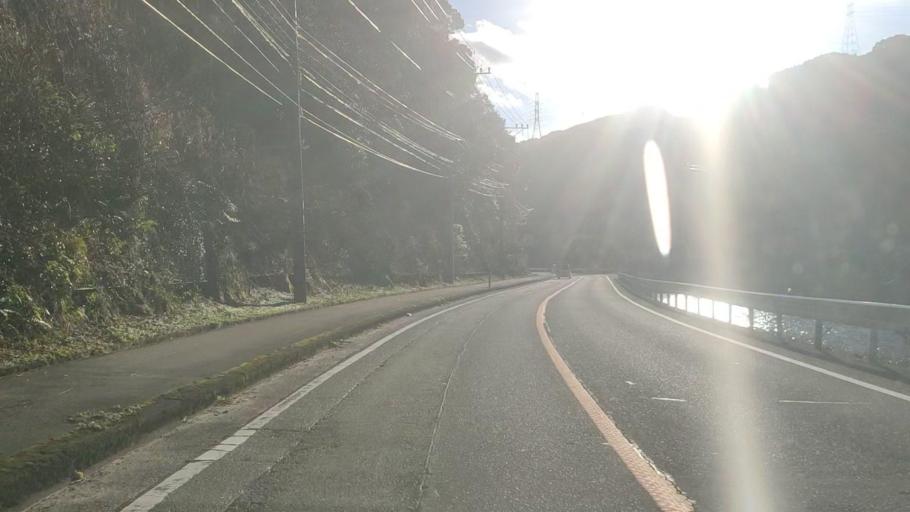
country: JP
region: Saga Prefecture
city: Saga-shi
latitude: 33.3475
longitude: 130.2491
